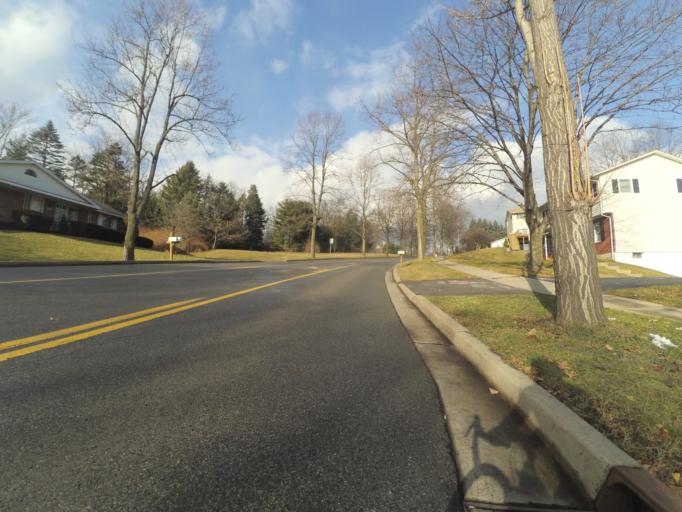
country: US
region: Pennsylvania
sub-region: Centre County
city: State College
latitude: 40.7871
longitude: -77.8387
